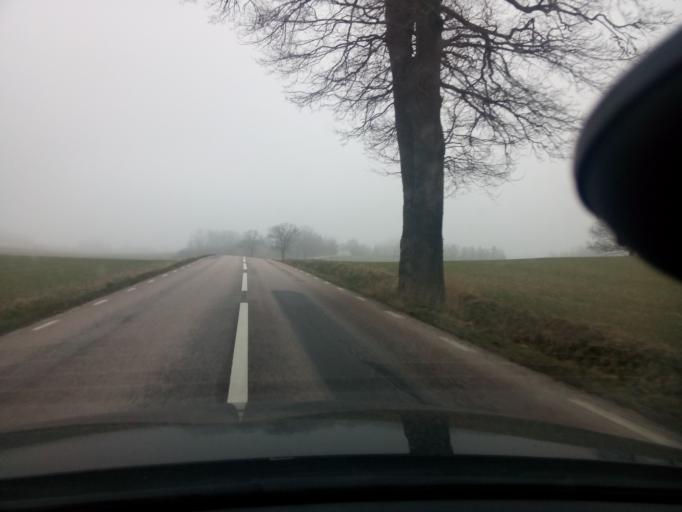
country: SE
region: Soedermanland
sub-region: Nykopings Kommun
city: Nykoping
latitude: 58.8940
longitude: 17.0944
